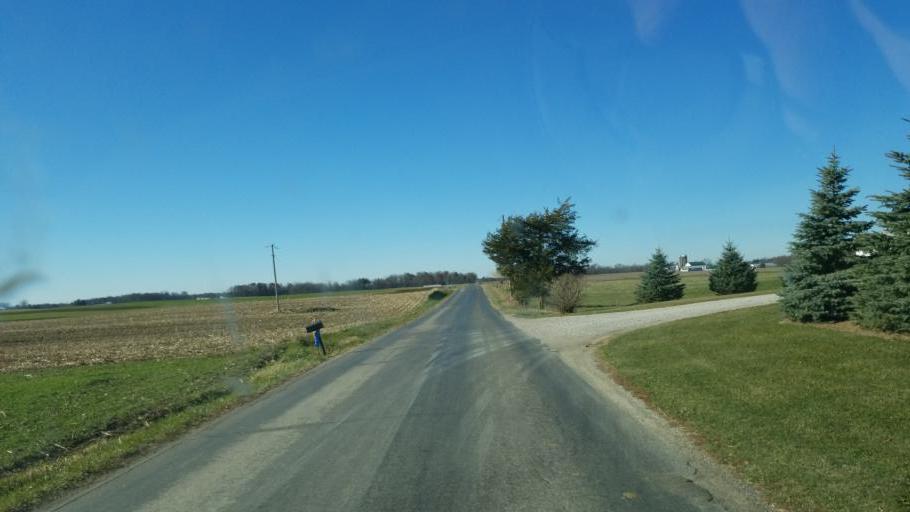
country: US
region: Ohio
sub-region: Huron County
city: Greenwich
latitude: 40.9604
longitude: -82.5571
